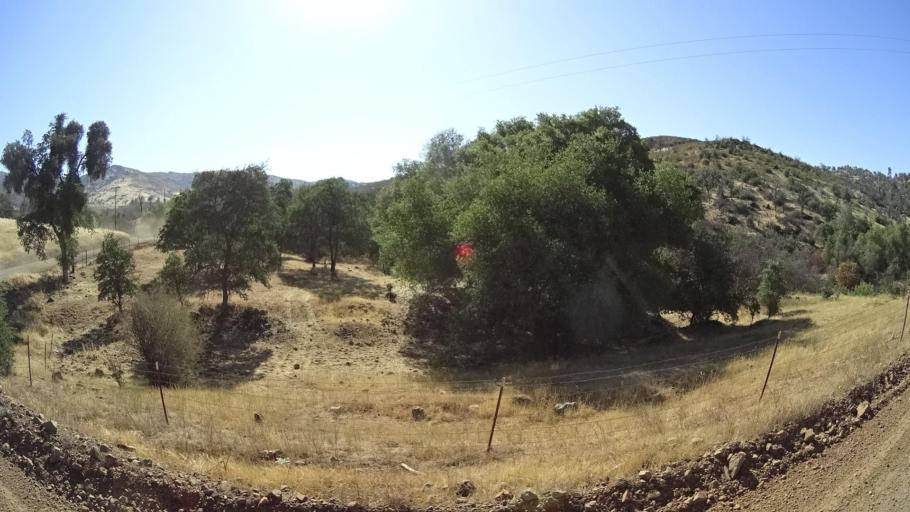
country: US
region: California
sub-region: Mariposa County
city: Mariposa
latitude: 37.6176
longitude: -120.2291
